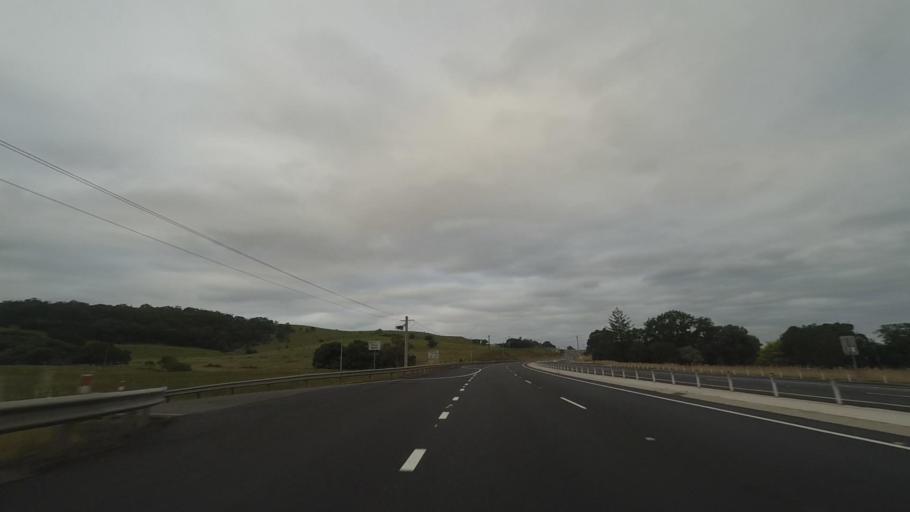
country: AU
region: New South Wales
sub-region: Kiama
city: Gerringong
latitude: -34.7499
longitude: 150.7888
